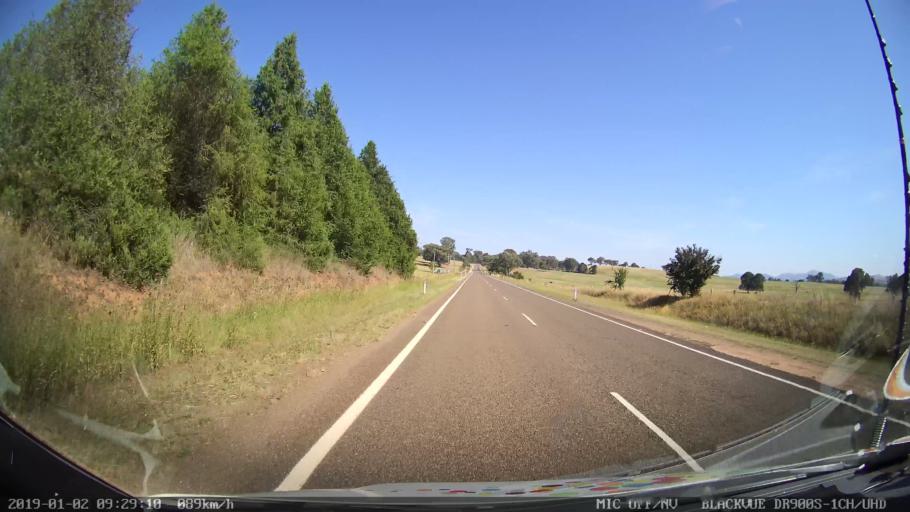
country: AU
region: New South Wales
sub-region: Tumut Shire
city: Tumut
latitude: -35.3416
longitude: 148.2451
